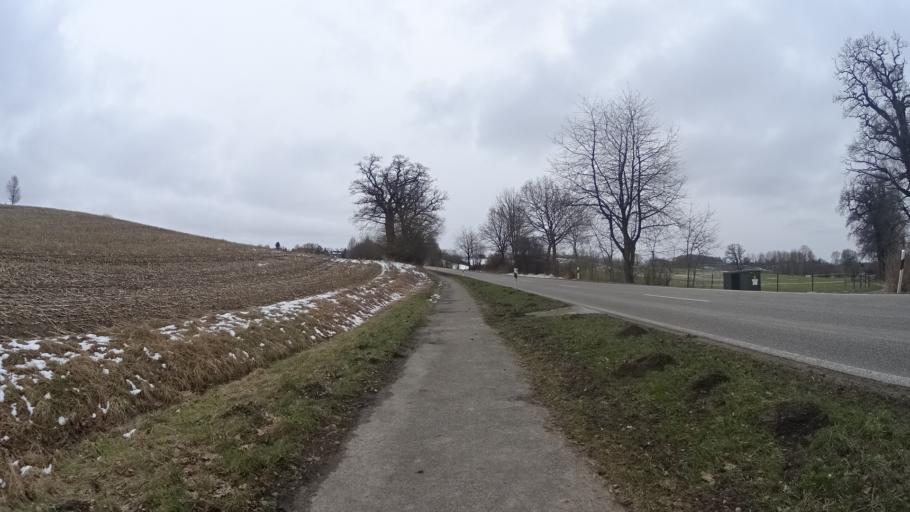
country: DE
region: Schleswig-Holstein
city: Lutjenburg
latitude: 54.2750
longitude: 10.5775
